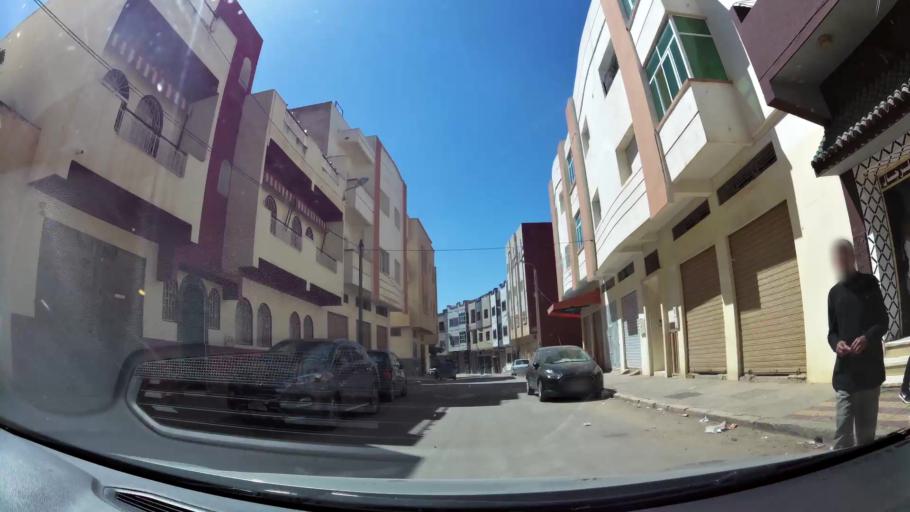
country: MA
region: Meknes-Tafilalet
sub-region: Meknes
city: Meknes
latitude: 33.8679
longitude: -5.5497
